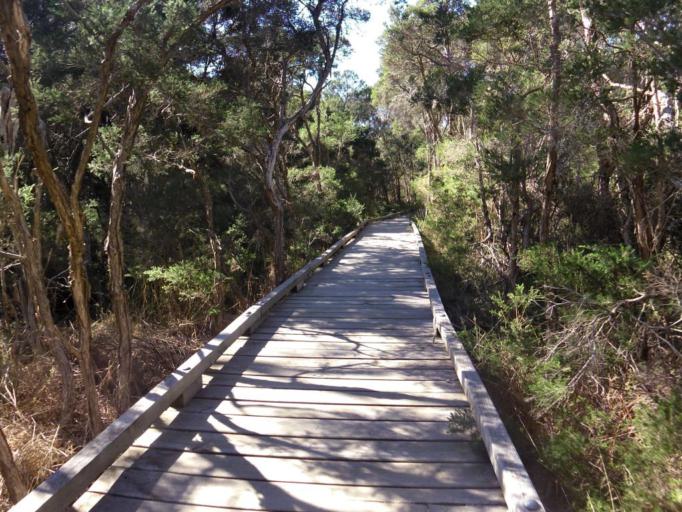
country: AU
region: Victoria
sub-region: Mornington Peninsula
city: Mount Martha
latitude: -38.2650
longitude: 145.0401
